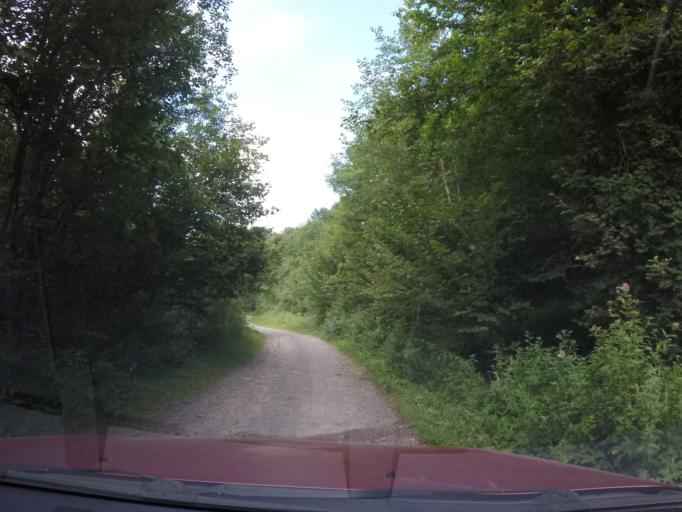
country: UA
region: Zakarpattia
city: Velykyi Bereznyi
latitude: 49.0188
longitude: 22.6316
